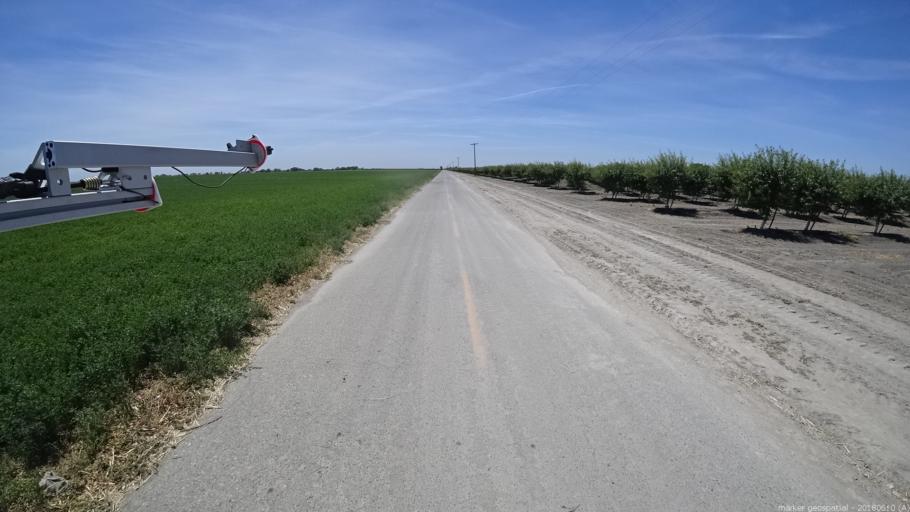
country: US
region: California
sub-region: Merced County
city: Dos Palos
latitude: 37.0375
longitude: -120.5288
